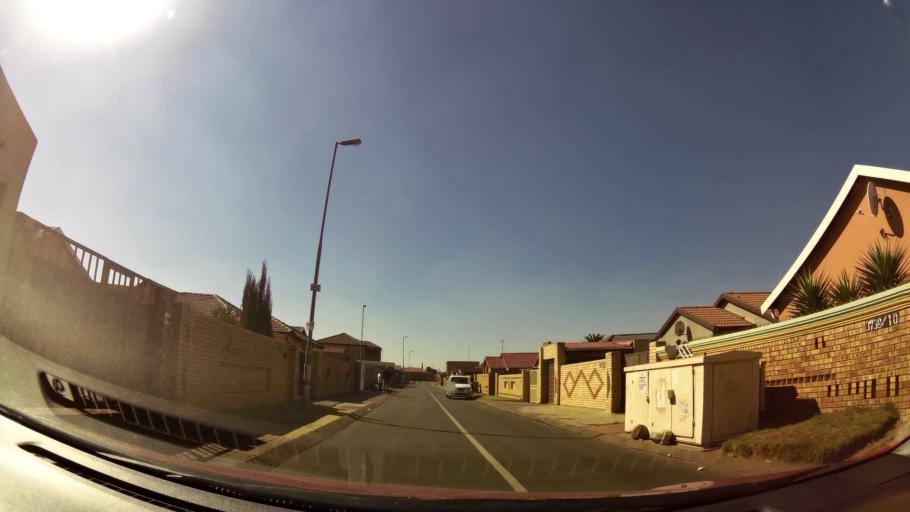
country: ZA
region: Gauteng
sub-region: City of Johannesburg Metropolitan Municipality
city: Soweto
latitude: -26.2395
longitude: 27.8381
